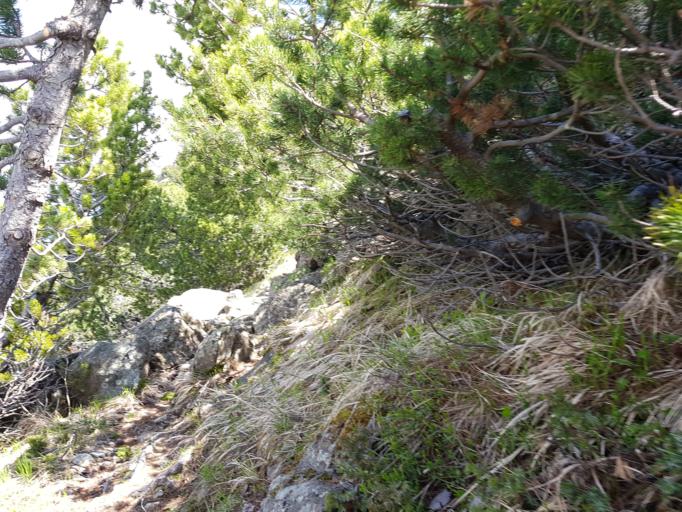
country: IT
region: Liguria
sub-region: Provincia di Genova
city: Santo Stefano d'Aveto
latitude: 44.5610
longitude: 9.5069
